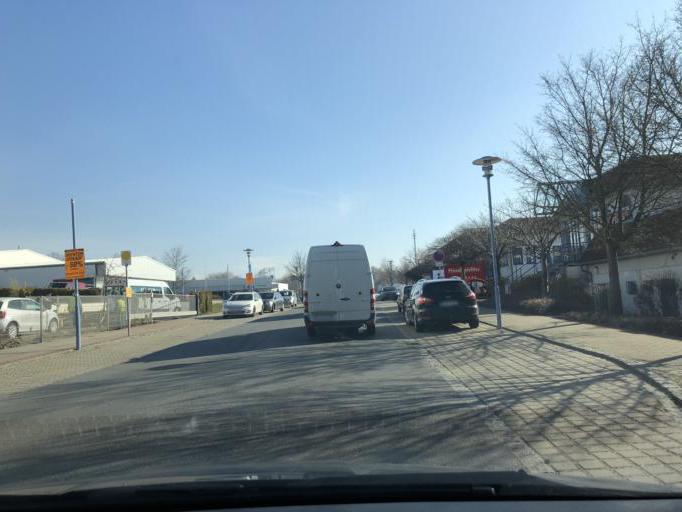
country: DE
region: Saxony
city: Bischofswerda
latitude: 51.1373
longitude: 14.1909
